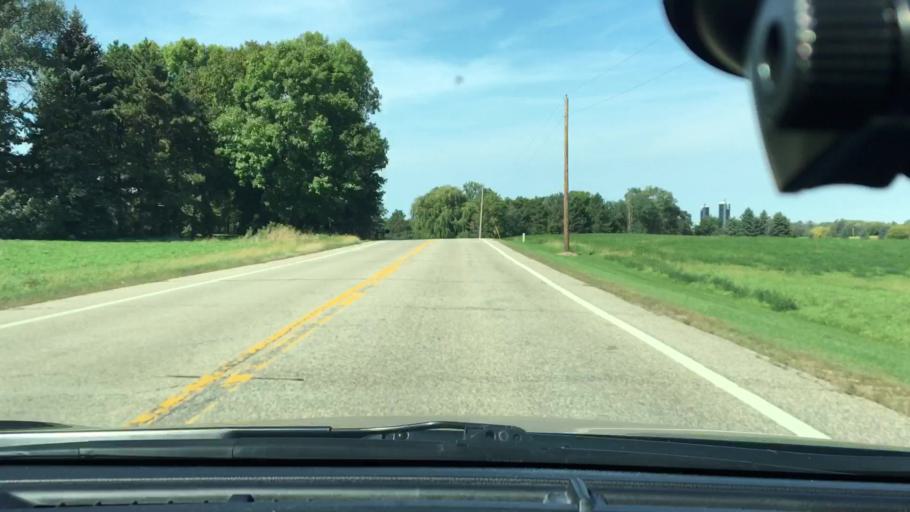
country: US
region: Minnesota
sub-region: Hennepin County
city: Corcoran
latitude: 45.1197
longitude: -93.6006
